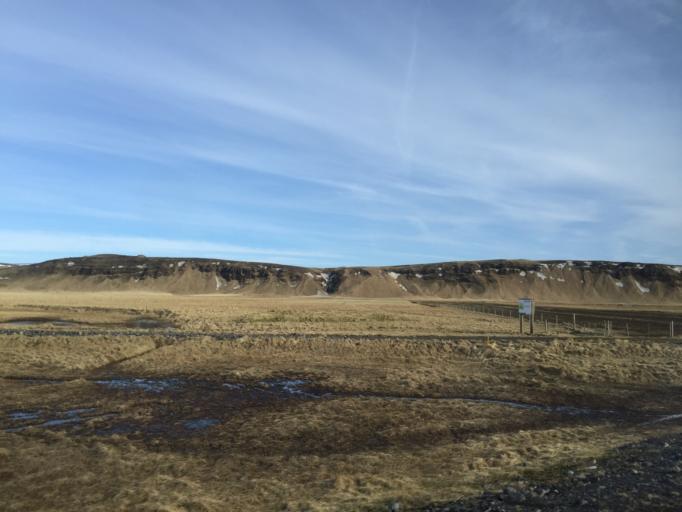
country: IS
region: South
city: Vestmannaeyjar
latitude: 63.4495
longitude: -19.2057
